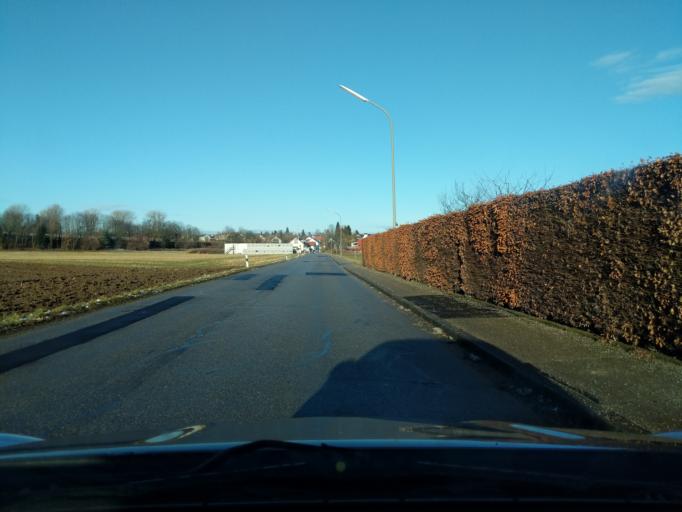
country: DE
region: Bavaria
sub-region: Upper Bavaria
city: Zorneding
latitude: 48.0914
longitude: 11.8408
